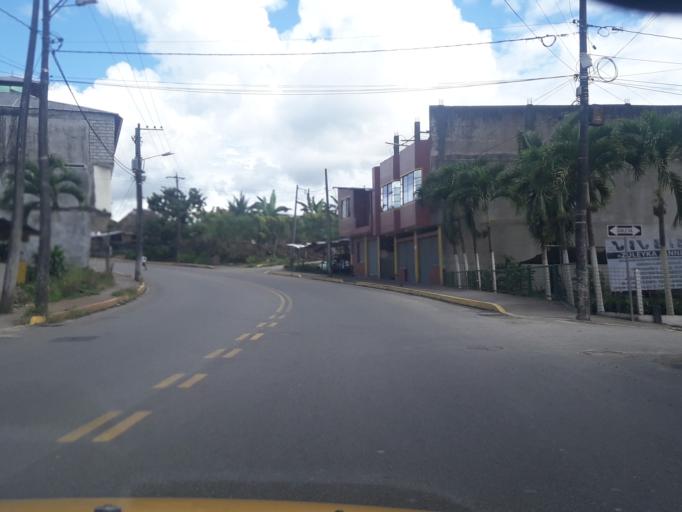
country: EC
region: Napo
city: Tena
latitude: -1.0041
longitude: -77.8179
